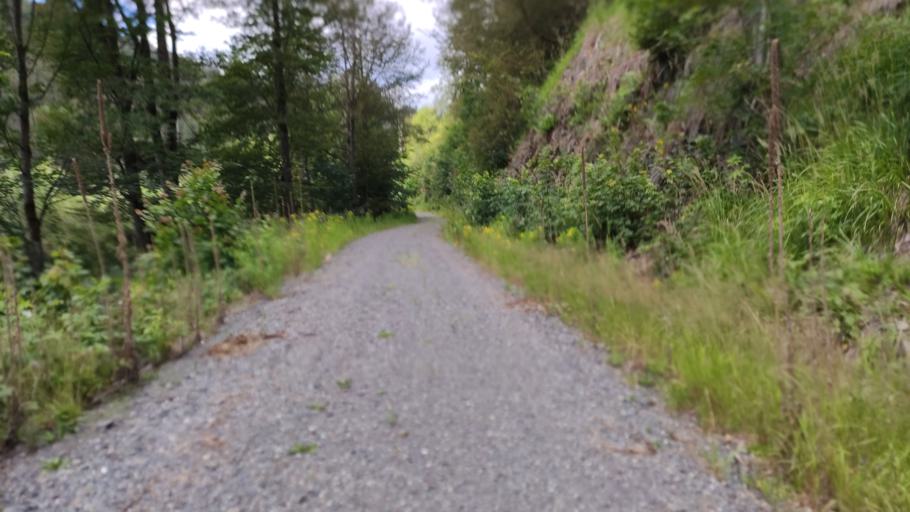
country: DE
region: Bavaria
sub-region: Upper Franconia
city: Nordhalben
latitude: 50.3681
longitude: 11.4823
